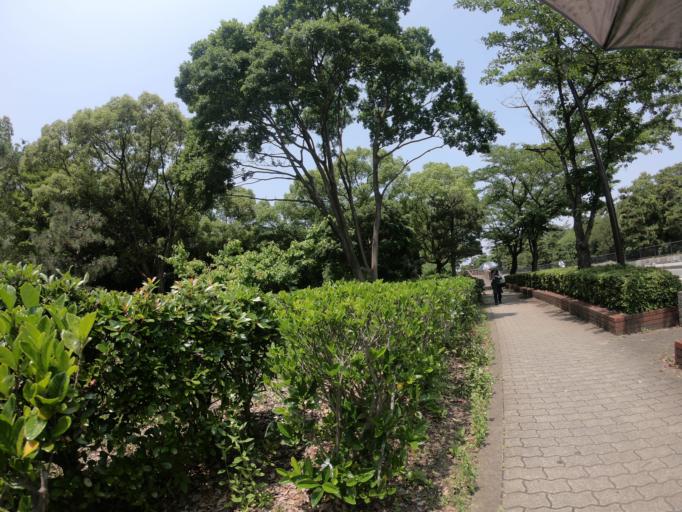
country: JP
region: Osaka
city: Sakai
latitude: 34.5611
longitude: 135.4841
